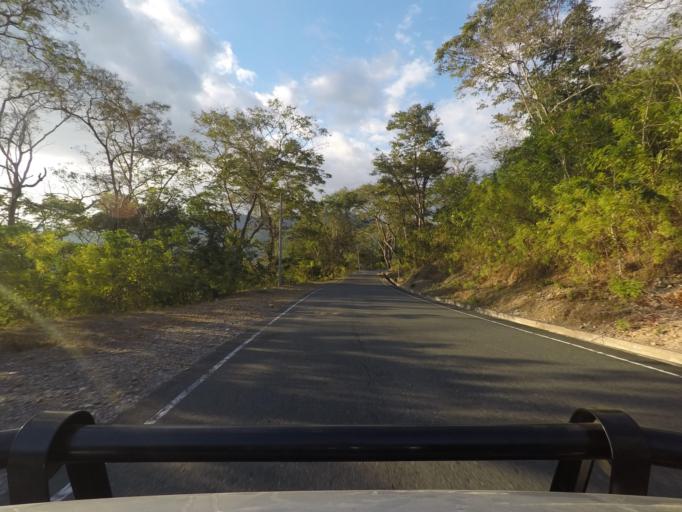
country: TL
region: Bobonaro
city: Maliana
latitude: -8.9513
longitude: 125.0919
